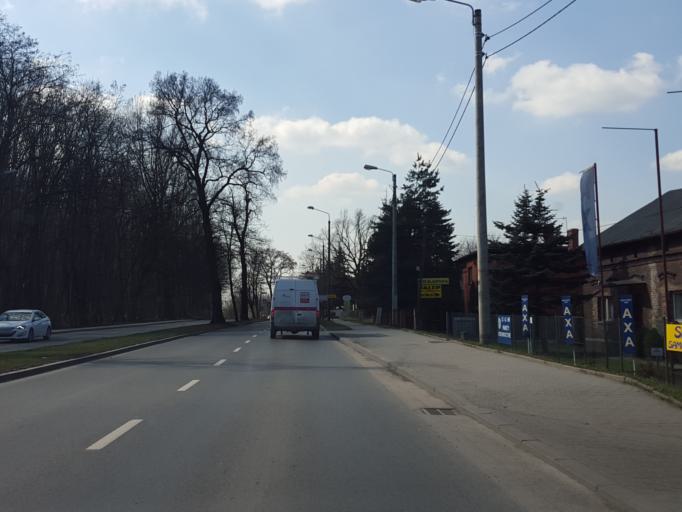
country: PL
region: Silesian Voivodeship
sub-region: Ruda Slaska
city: Ruda Slaska
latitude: 50.2542
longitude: 18.8532
